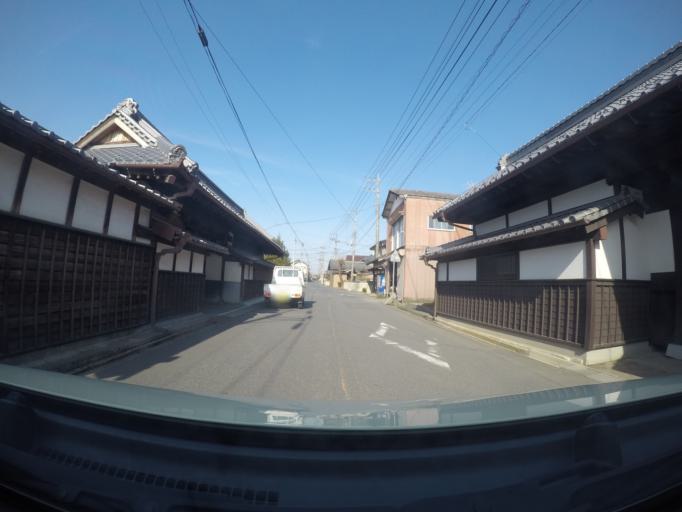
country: JP
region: Ibaraki
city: Tsukuba
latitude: 36.2232
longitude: 140.0660
